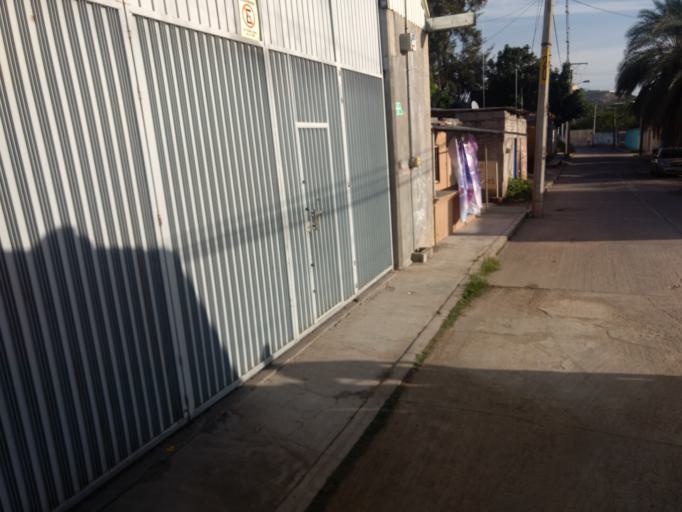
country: MX
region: Oaxaca
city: Ciudad de Huajuapam de Leon
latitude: 17.8150
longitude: -97.7881
